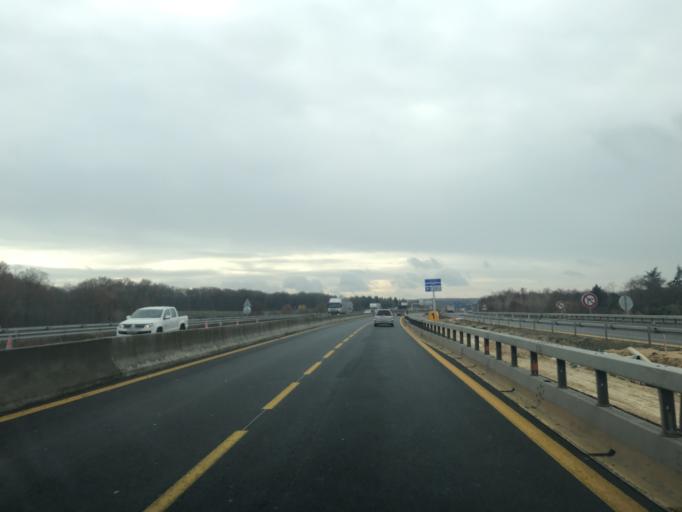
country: FR
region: Centre
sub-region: Departement d'Indre-et-Loire
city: Montbazon
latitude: 47.3003
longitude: 0.6920
